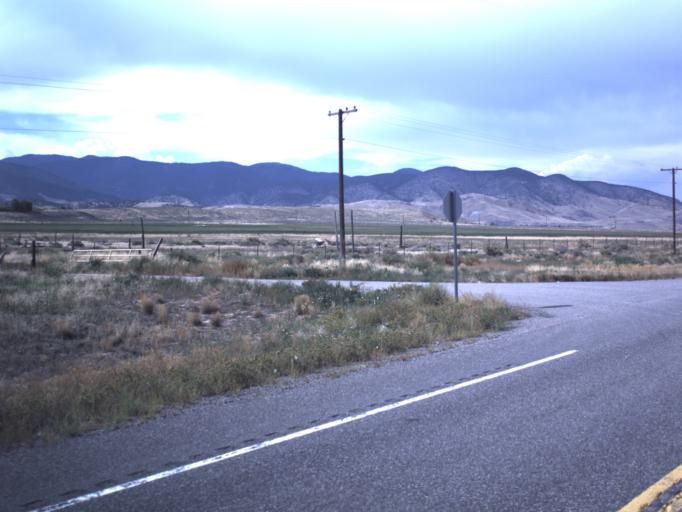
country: US
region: Utah
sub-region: Piute County
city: Junction
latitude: 38.4162
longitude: -112.2314
